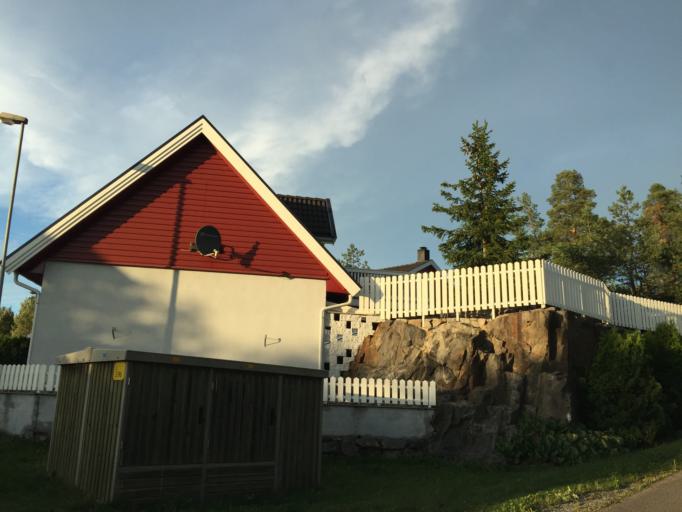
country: NO
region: Akershus
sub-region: Ski
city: Ski
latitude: 59.7616
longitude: 10.8510
